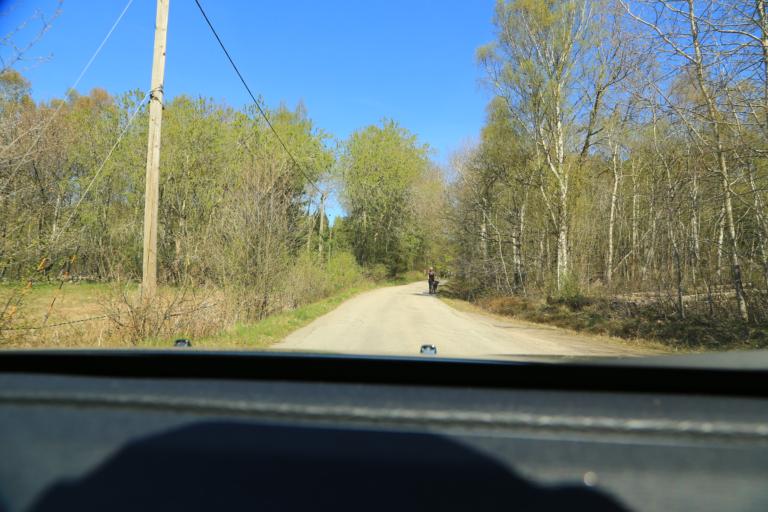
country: SE
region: Halland
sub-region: Varbergs Kommun
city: Traslovslage
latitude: 57.0928
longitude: 12.2891
